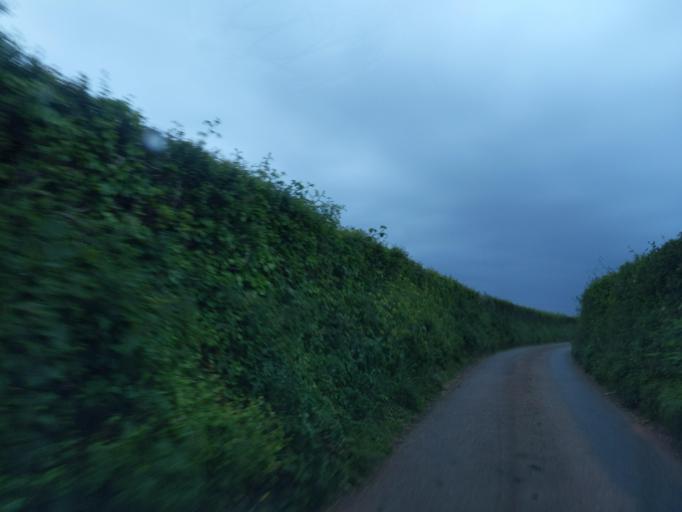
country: GB
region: England
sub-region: Borough of Torbay
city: Brixham
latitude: 50.3600
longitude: -3.5325
